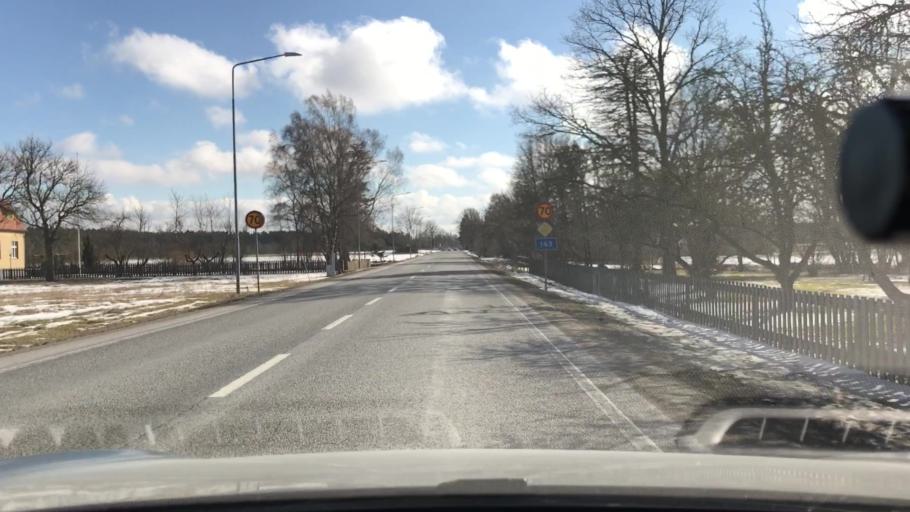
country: SE
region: Gotland
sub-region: Gotland
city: Visby
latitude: 57.5265
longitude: 18.4404
